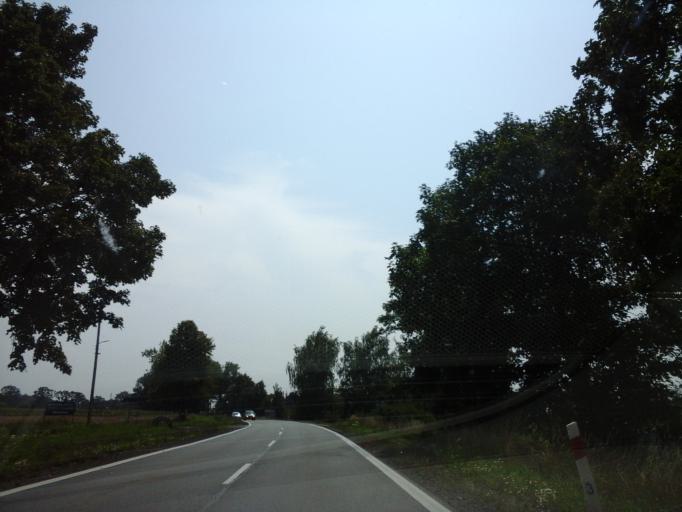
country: PL
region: Lower Silesian Voivodeship
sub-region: Powiat wroclawski
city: Zerniki Wroclawskie
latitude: 51.0250
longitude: 17.0615
